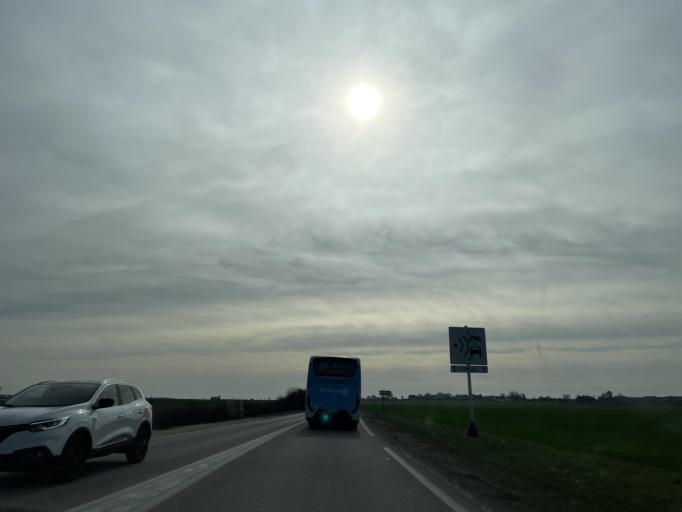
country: FR
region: Ile-de-France
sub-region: Departement de Seine-et-Marne
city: Jouy-le-Chatel
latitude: 48.6817
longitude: 3.1078
